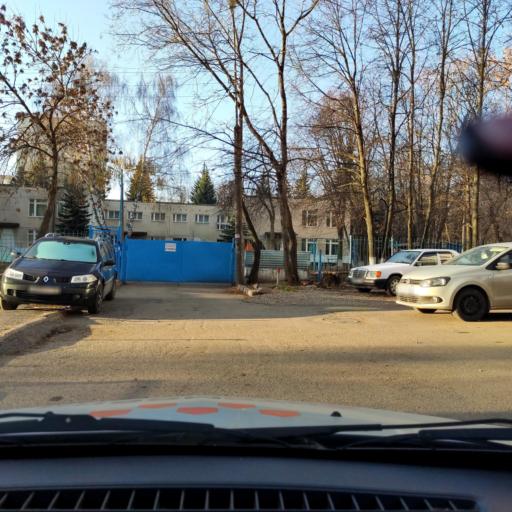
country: RU
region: Bashkortostan
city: Ufa
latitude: 54.7586
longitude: 55.9921
